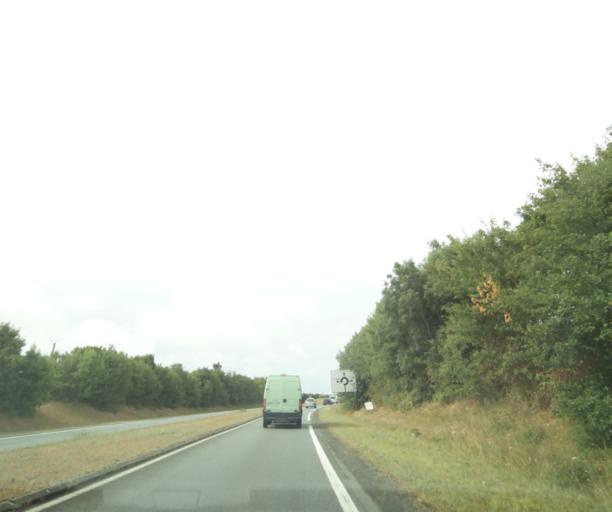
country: FR
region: Poitou-Charentes
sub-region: Departement de la Charente-Maritime
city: Marsilly
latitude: 46.2122
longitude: -1.1346
